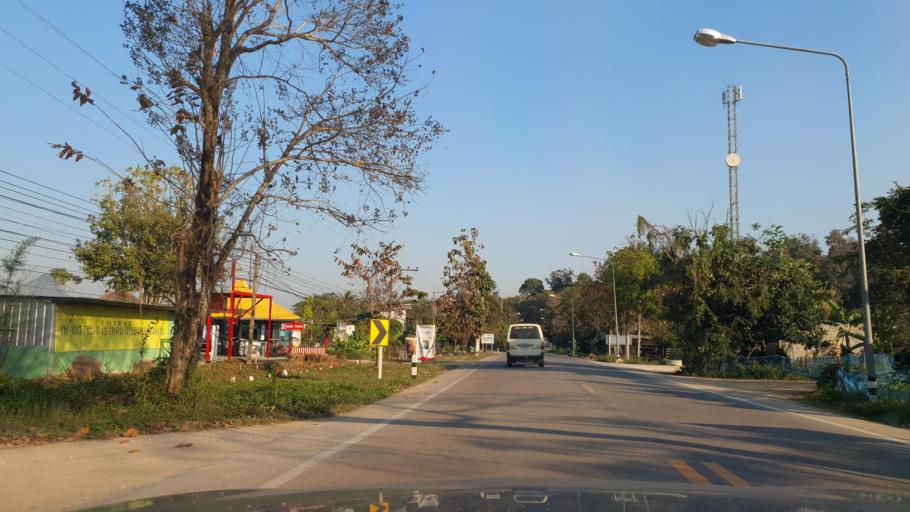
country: TH
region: Chiang Rai
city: Mae Lao
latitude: 19.8340
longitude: 99.7006
